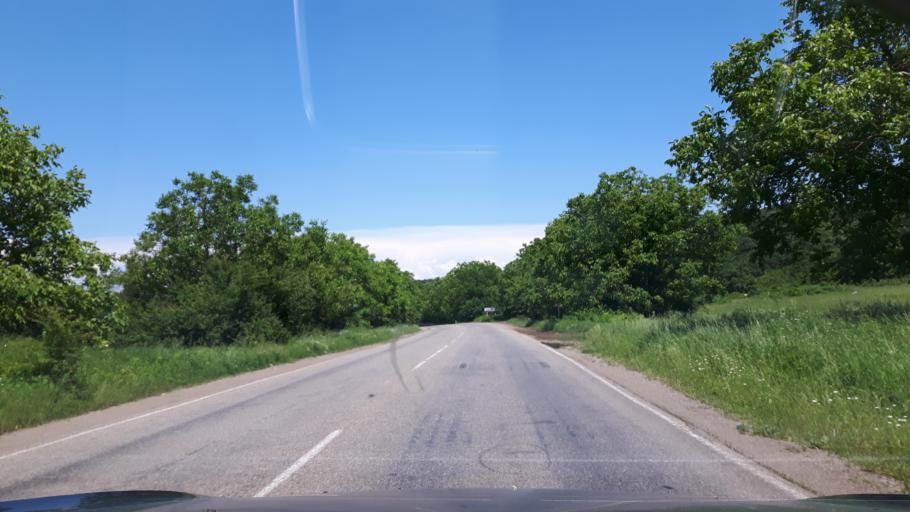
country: GE
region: Kakheti
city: Sighnaghi
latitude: 41.6354
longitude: 45.8242
